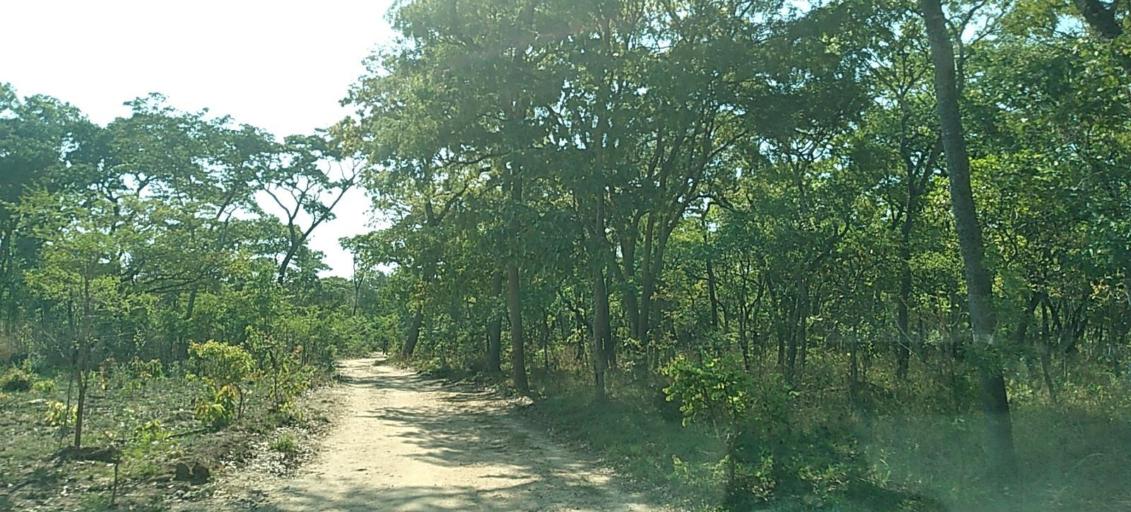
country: ZM
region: Central
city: Mkushi
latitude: -13.4707
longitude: 28.9758
